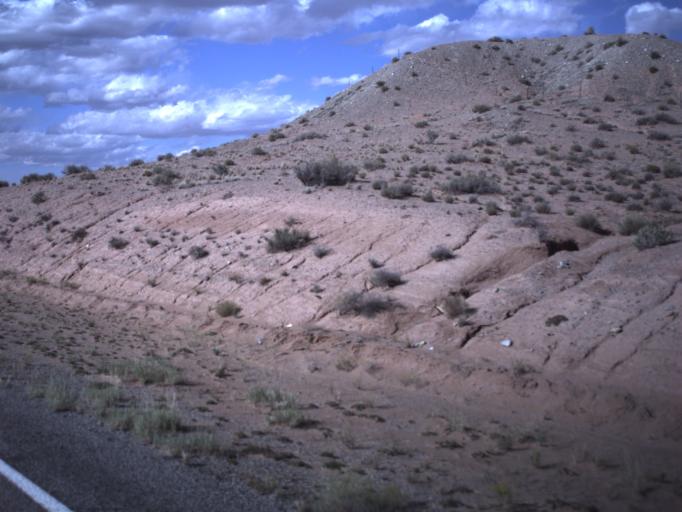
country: US
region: Utah
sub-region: Emery County
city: Ferron
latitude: 38.3392
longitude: -110.6897
